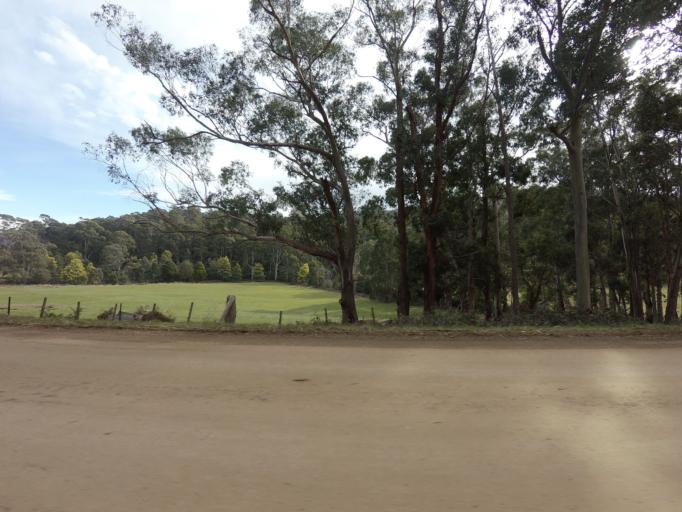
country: AU
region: Tasmania
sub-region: Huon Valley
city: Huonville
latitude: -43.0737
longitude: 147.0767
